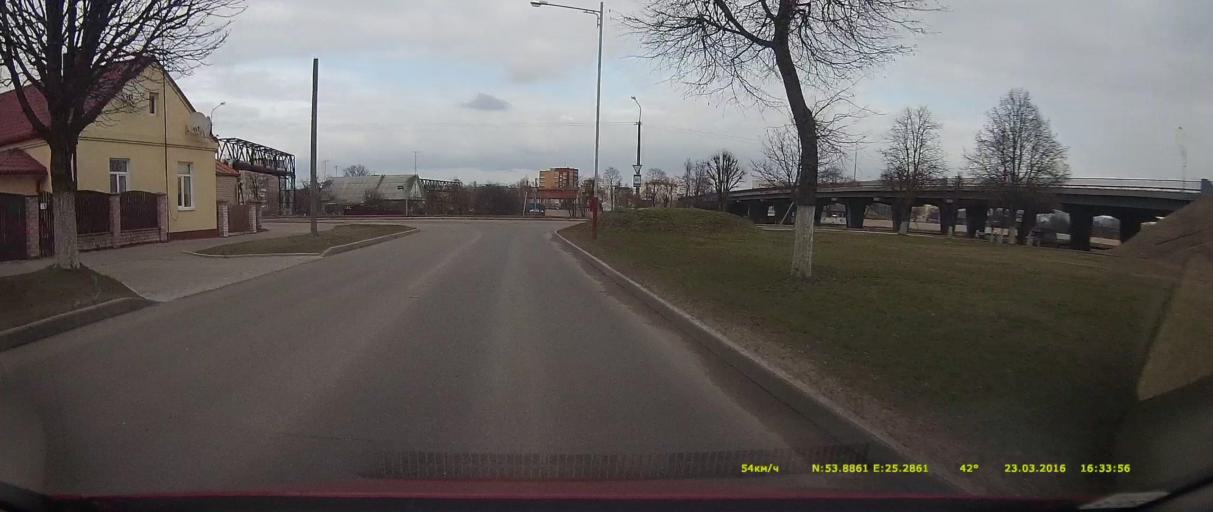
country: BY
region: Grodnenskaya
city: Lida
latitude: 53.8864
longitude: 25.2864
